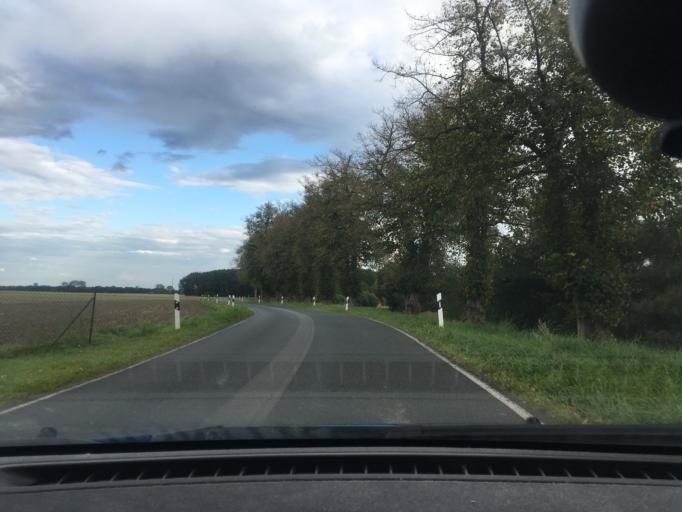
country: DE
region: Mecklenburg-Vorpommern
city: Boizenburg
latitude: 53.3559
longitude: 10.8338
